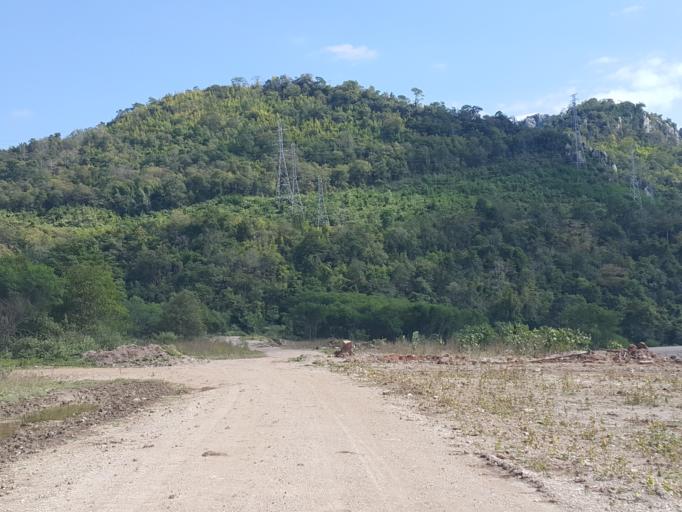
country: TH
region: Lampang
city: Mae Mo
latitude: 18.3281
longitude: 99.7610
